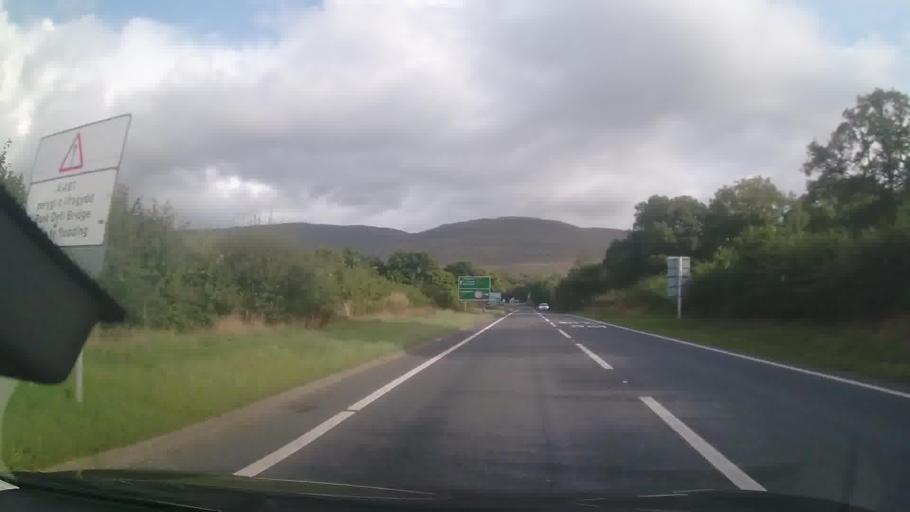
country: GB
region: Wales
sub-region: Gwynedd
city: Dolgellau
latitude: 52.7358
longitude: -3.8309
